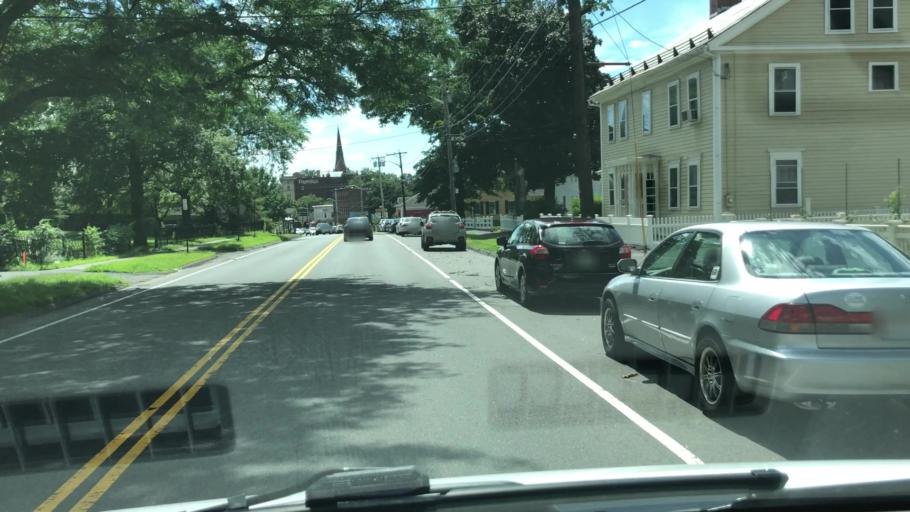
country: US
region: Massachusetts
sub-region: Hampshire County
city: Northampton
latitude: 42.3223
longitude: -72.6260
